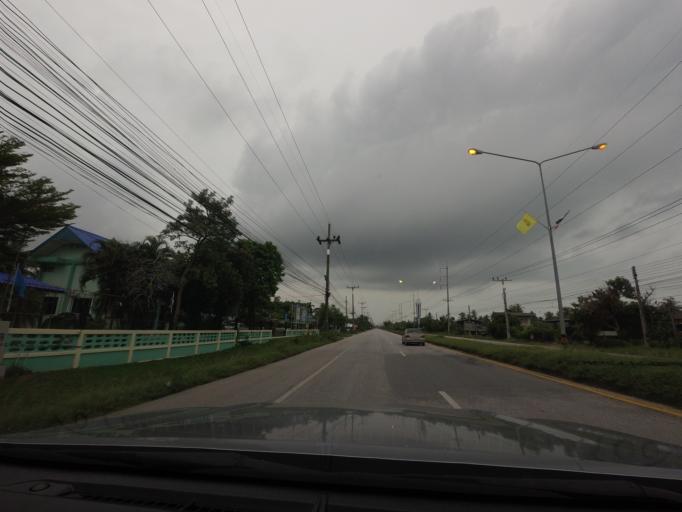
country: TH
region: Songkhla
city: Sathing Phra
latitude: 7.4260
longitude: 100.4560
